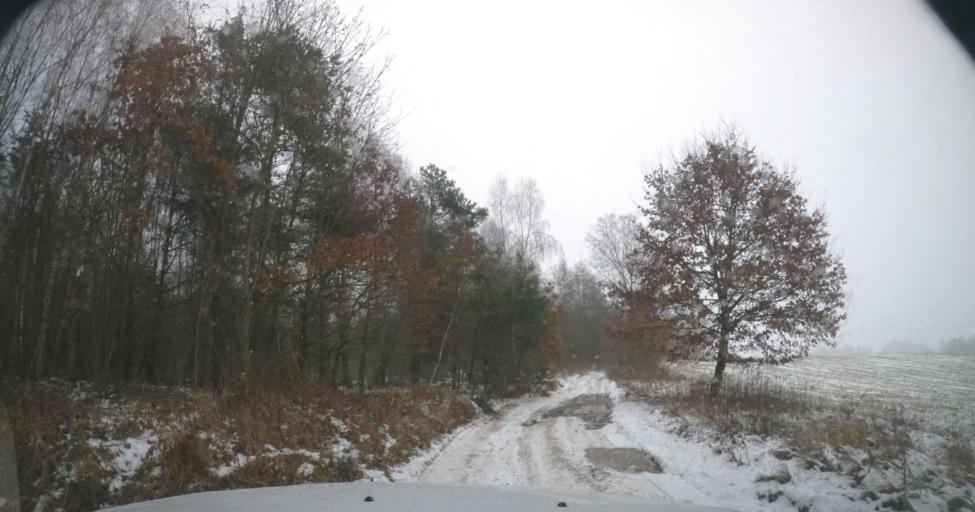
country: PL
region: West Pomeranian Voivodeship
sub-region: Powiat kamienski
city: Golczewo
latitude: 53.8710
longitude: 15.0546
